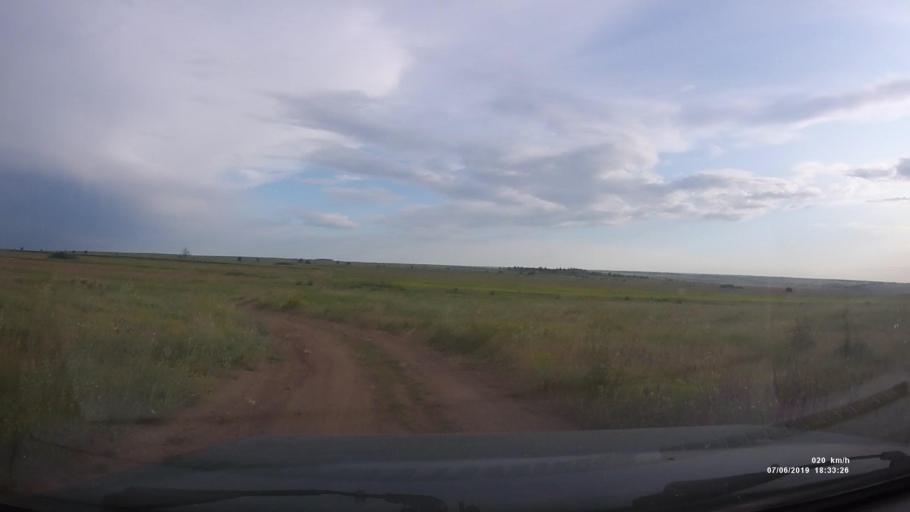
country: RU
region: Rostov
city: Staraya Stanitsa
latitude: 48.2615
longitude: 40.3626
